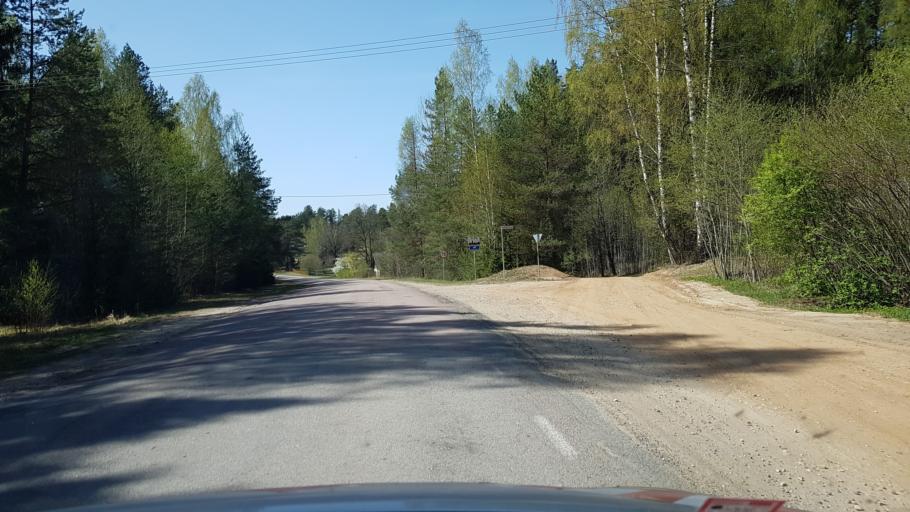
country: EE
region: Tartu
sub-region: Elva linn
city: Elva
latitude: 58.2426
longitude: 26.4245
